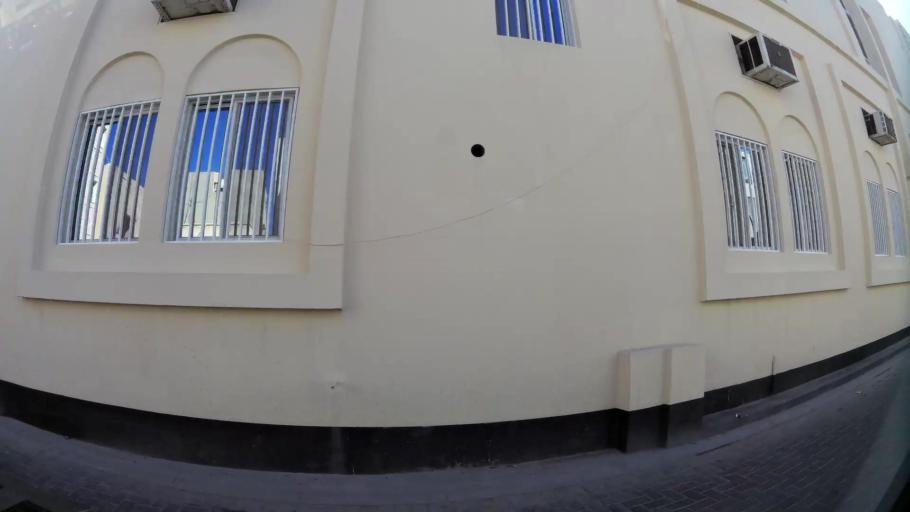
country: BH
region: Muharraq
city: Al Hadd
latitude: 26.2423
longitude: 50.6532
